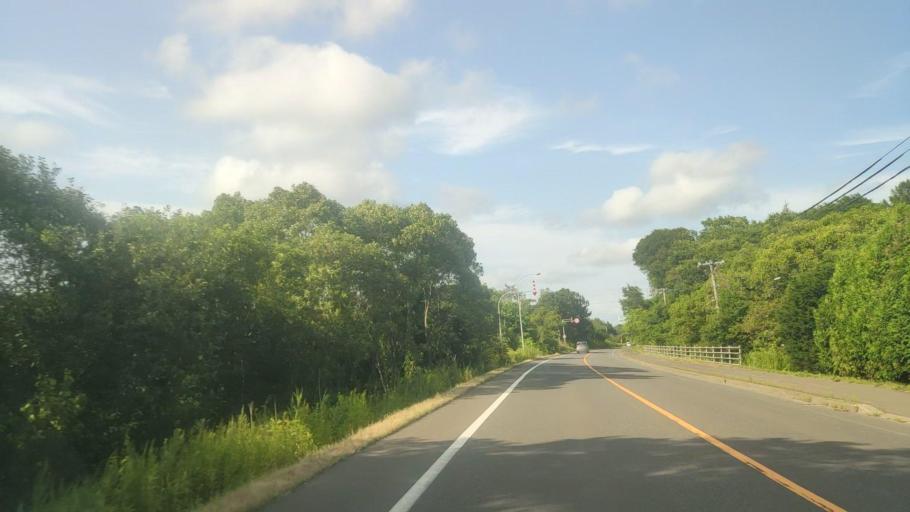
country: JP
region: Hokkaido
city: Chitose
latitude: 42.7338
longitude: 141.7763
